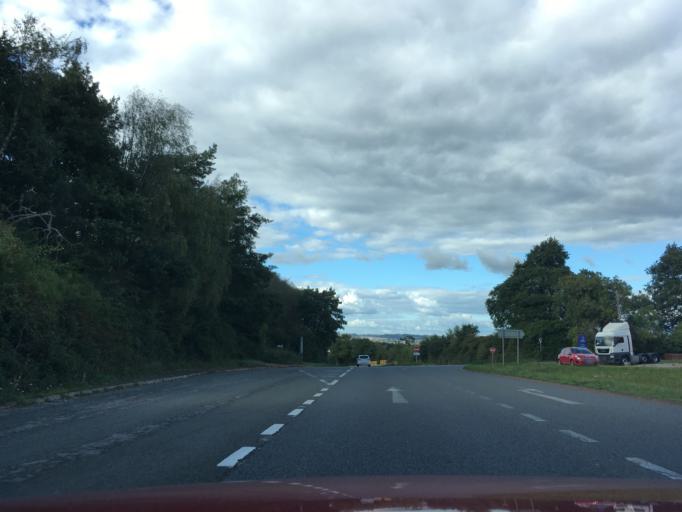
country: GB
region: England
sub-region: Devon
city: Exminster
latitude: 50.6795
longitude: -3.5318
